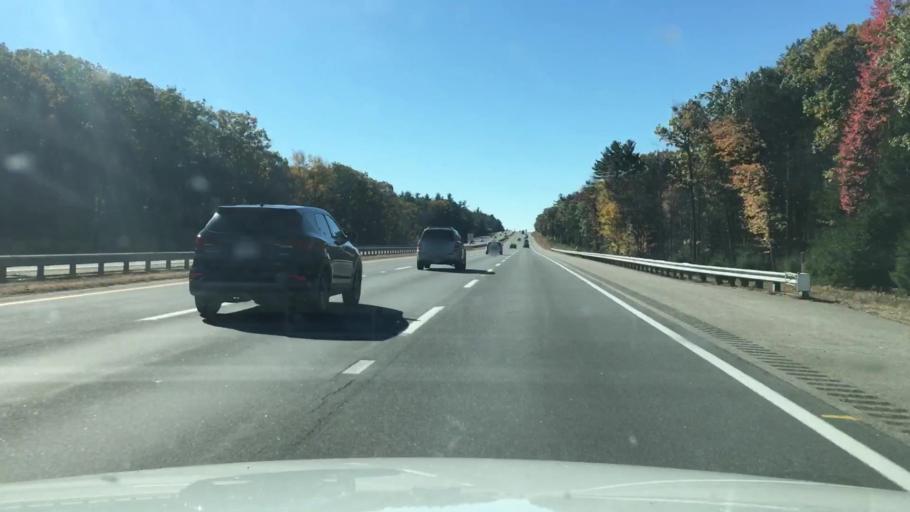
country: US
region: Maine
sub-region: York County
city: Wells Beach Station
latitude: 43.2907
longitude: -70.6168
